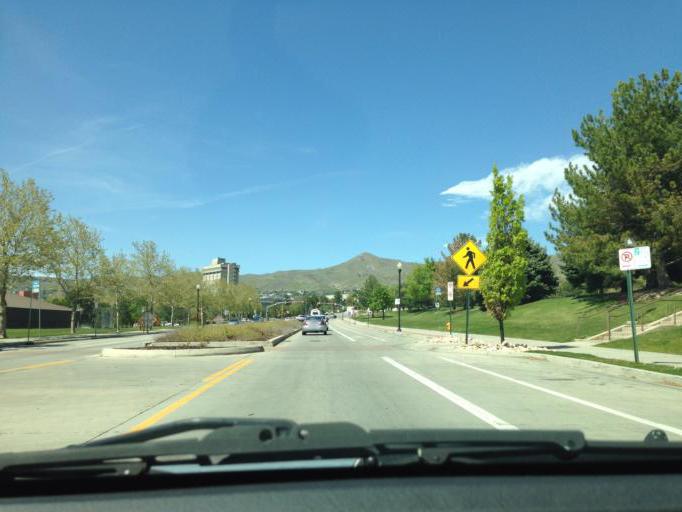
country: US
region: Utah
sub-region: Salt Lake County
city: Salt Lake City
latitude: 40.7564
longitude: -111.8453
